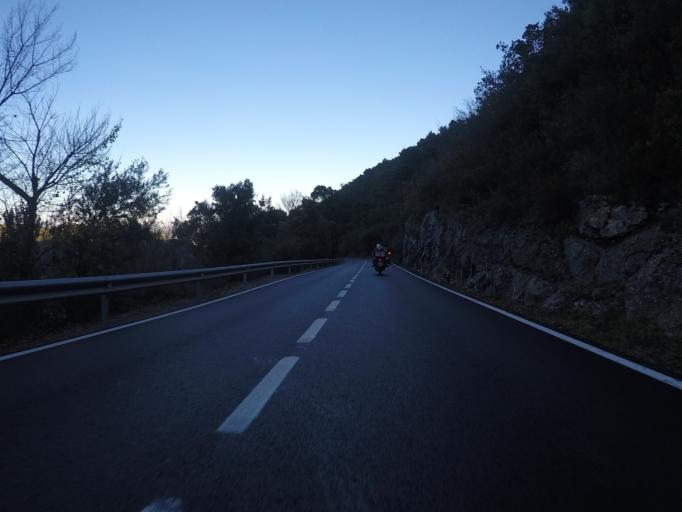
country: ES
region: Catalonia
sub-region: Provincia de Barcelona
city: Monistrol de Montserrat
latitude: 41.6123
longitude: 1.8270
